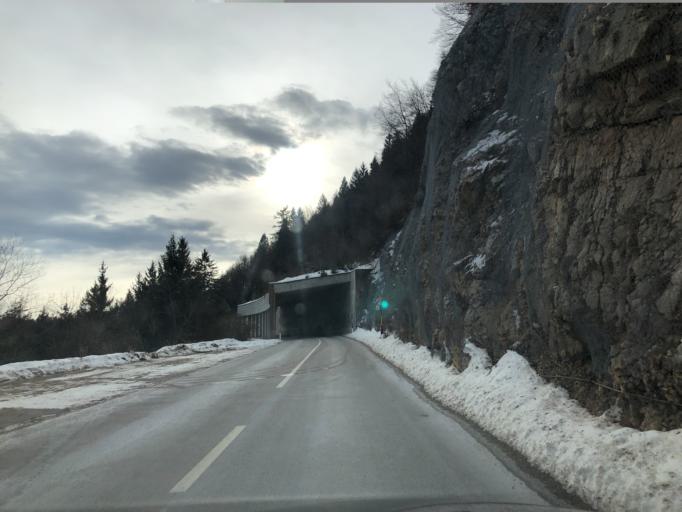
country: IT
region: Trentino-Alto Adige
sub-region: Provincia di Trento
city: Lasino
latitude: 46.0293
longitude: 11.0304
